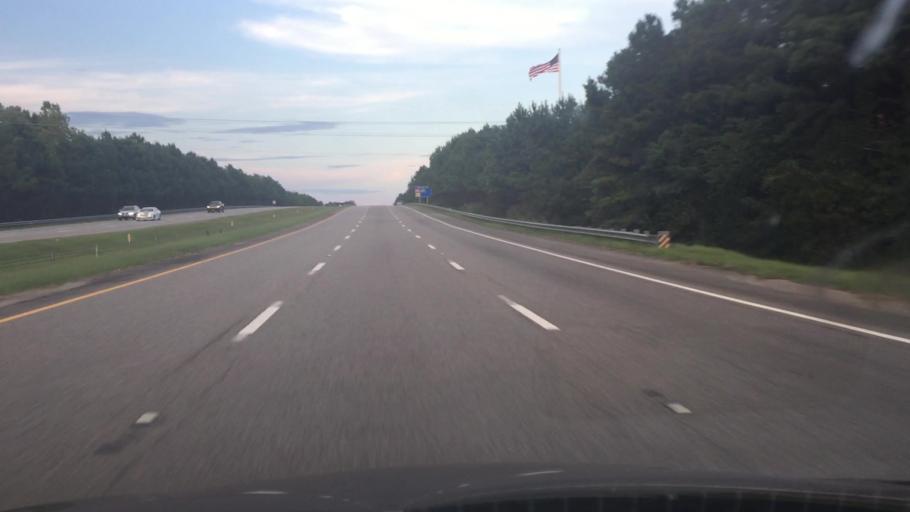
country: US
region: South Carolina
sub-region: Horry County
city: Myrtle Beach
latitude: 33.7499
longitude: -78.8726
